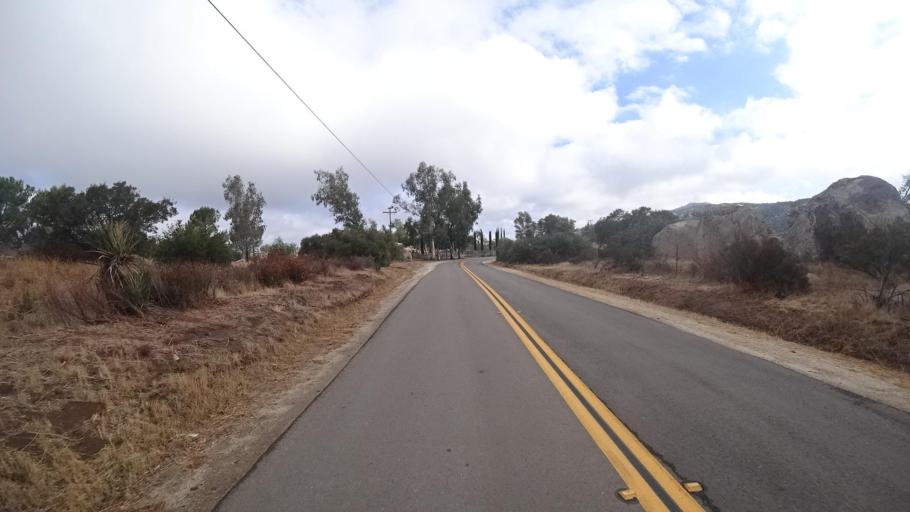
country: MX
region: Baja California
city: Tecate
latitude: 32.6098
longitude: -116.5763
